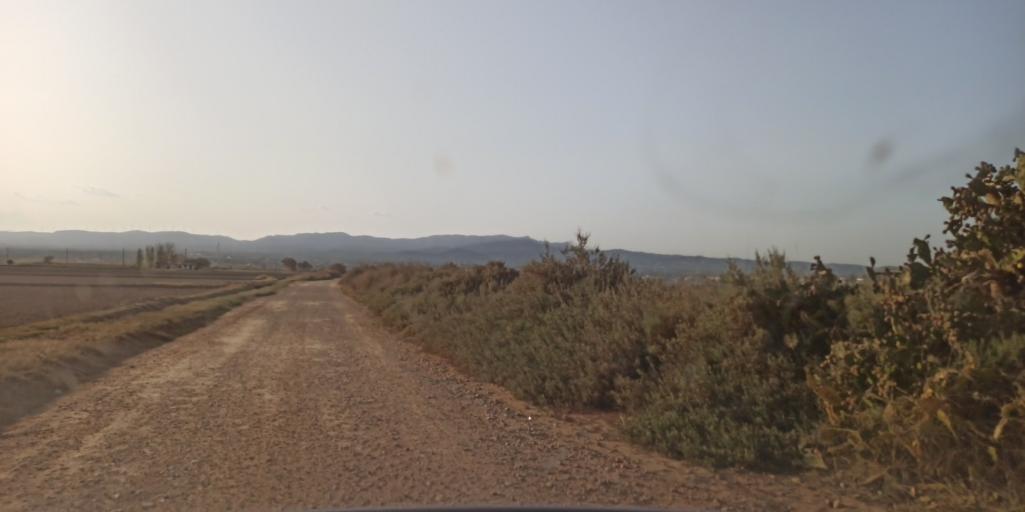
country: ES
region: Catalonia
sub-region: Provincia de Tarragona
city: L'Ampolla
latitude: 40.7801
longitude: 0.7161
